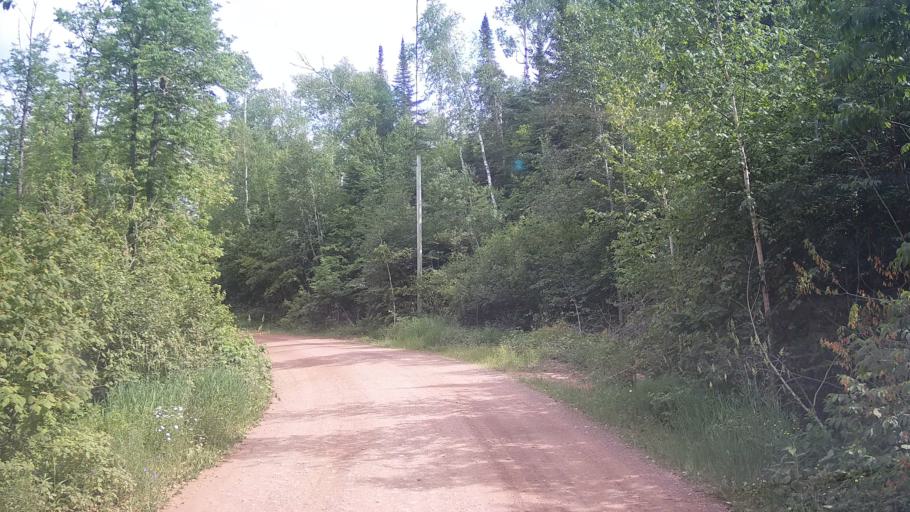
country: CA
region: Ontario
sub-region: Thunder Bay District
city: Thunder Bay
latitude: 48.6661
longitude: -88.6655
